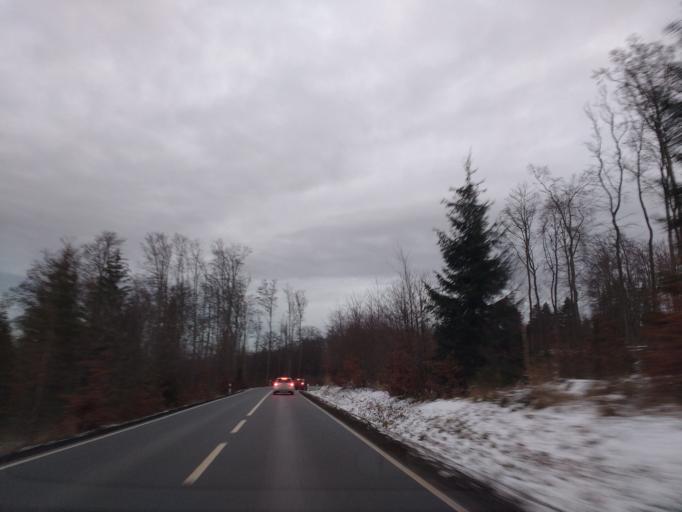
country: DE
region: Saxony-Anhalt
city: Friedrichsbrunn
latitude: 51.7006
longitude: 11.0559
